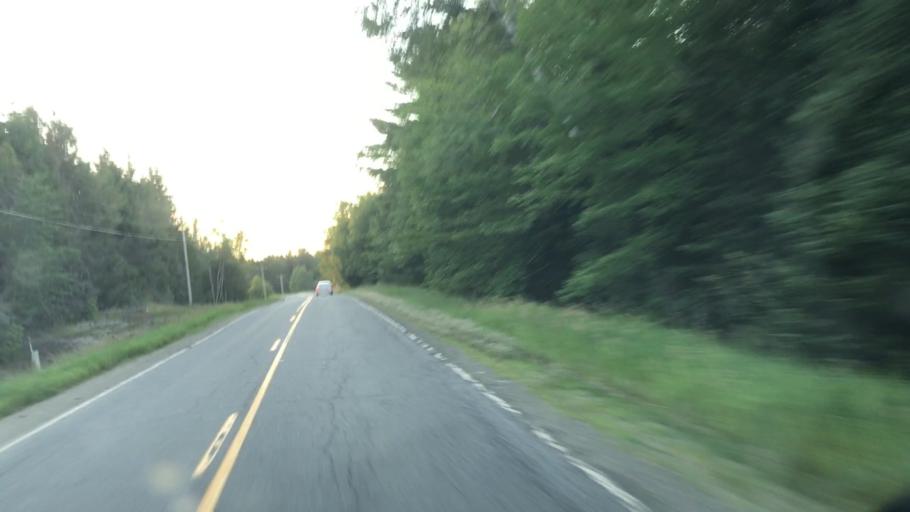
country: US
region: Maine
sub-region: Penobscot County
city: Medway
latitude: 45.6043
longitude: -68.2531
